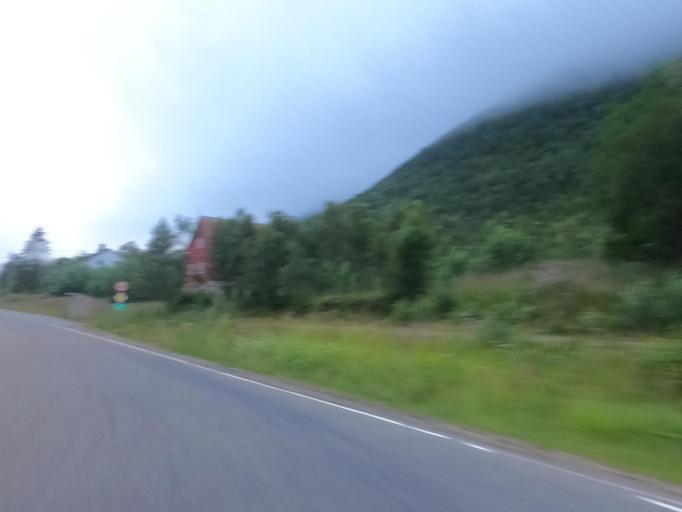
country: NO
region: Nordland
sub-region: Lodingen
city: Lodingen
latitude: 68.6179
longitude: 15.7599
